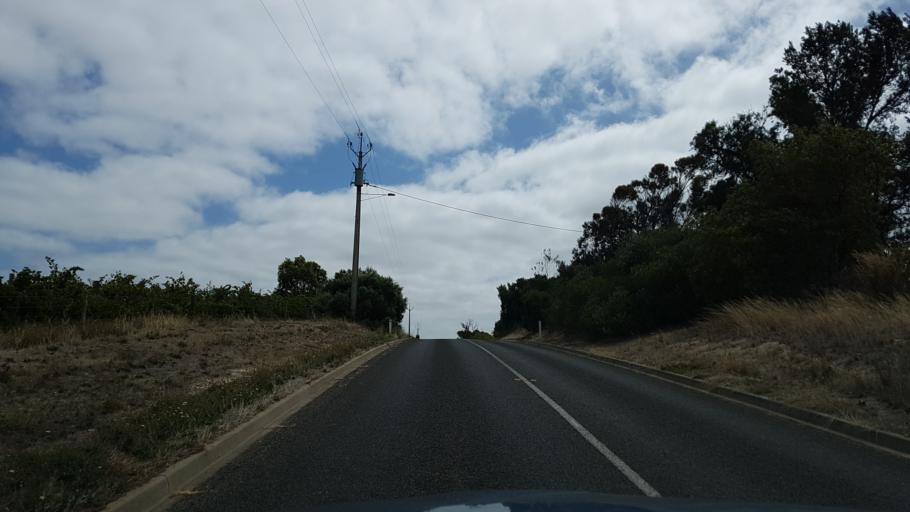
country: AU
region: South Australia
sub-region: Onkaparinga
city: McLaren Vale
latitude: -35.2188
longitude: 138.5180
